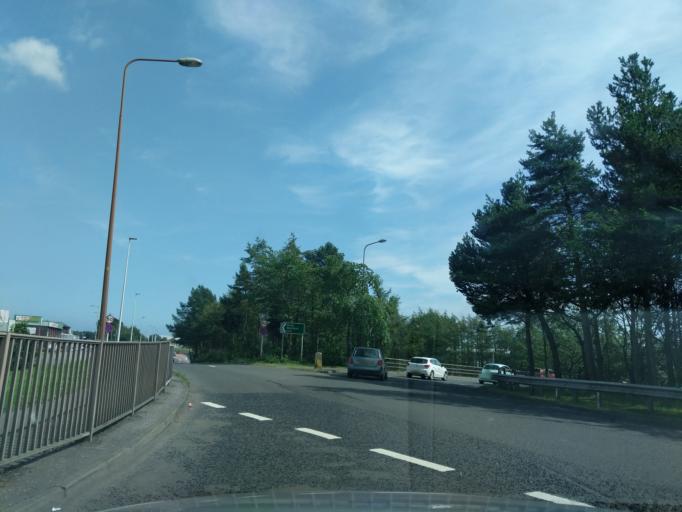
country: GB
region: Scotland
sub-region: Dundee City
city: Dundee
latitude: 56.4822
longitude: -3.0184
